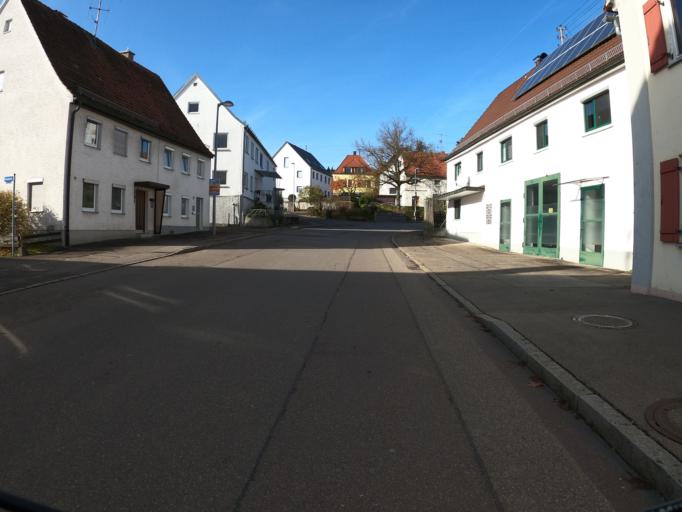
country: DE
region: Bavaria
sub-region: Swabia
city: Nersingen
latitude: 48.4596
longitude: 10.1040
